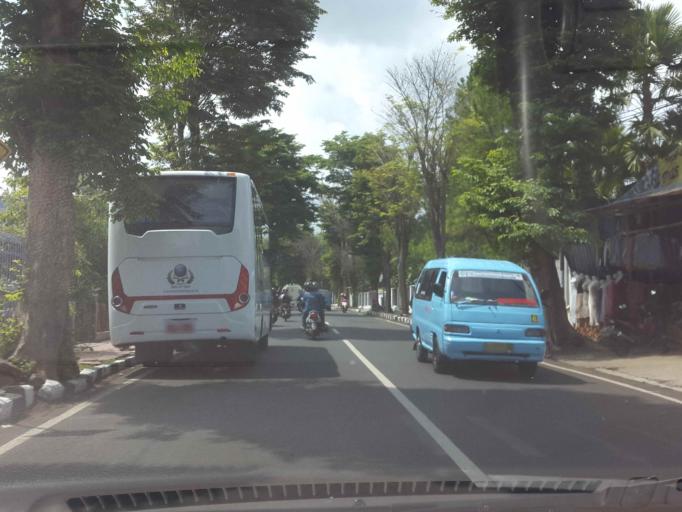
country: ID
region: Central Java
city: Salatiga
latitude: -7.3357
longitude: 110.5081
